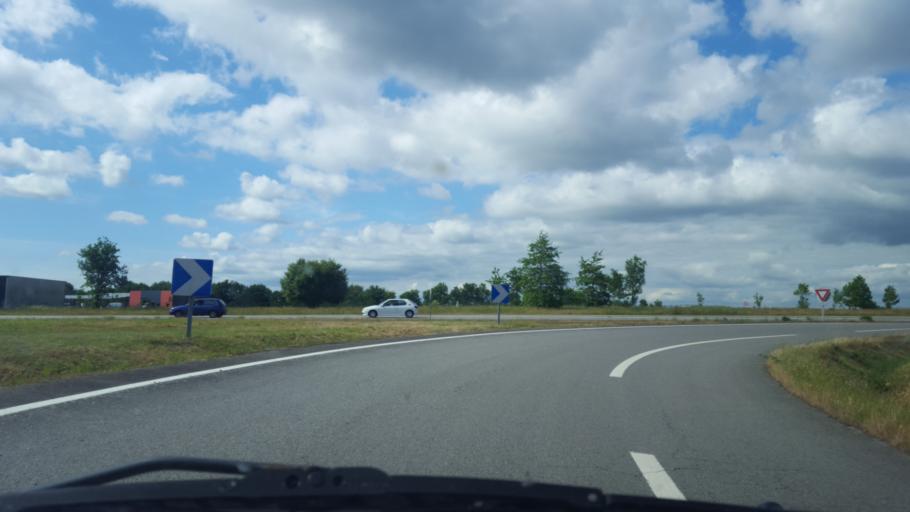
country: FR
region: Pays de la Loire
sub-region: Departement de la Loire-Atlantique
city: Paulx
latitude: 46.9983
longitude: -1.7387
